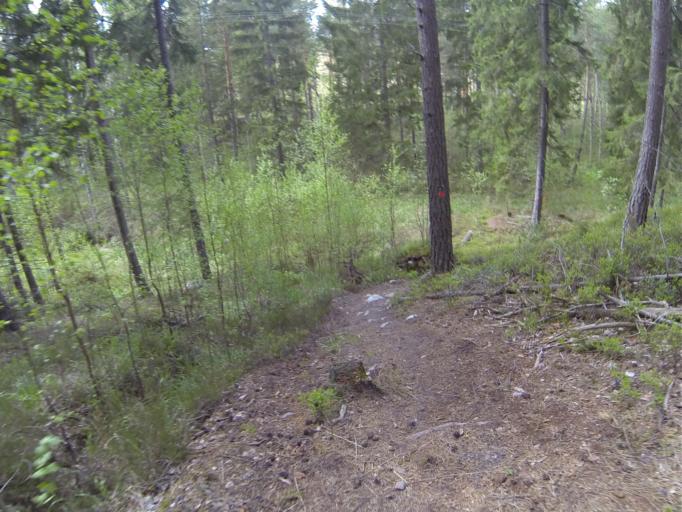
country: FI
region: Varsinais-Suomi
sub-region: Salo
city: Halikko
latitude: 60.3291
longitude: 23.0705
